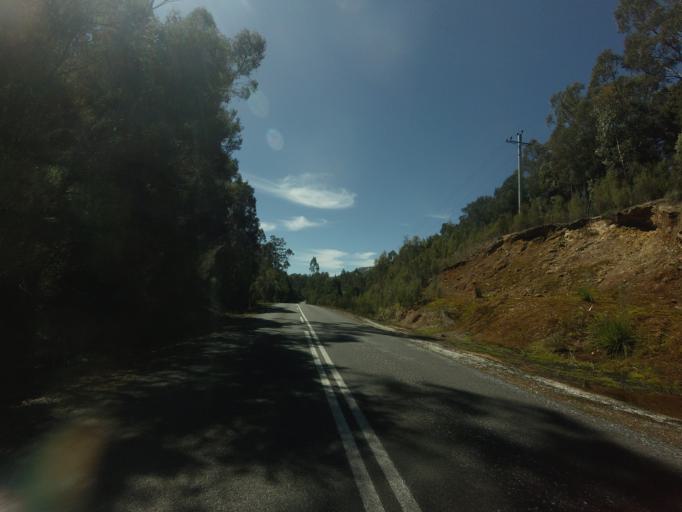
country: AU
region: Tasmania
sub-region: West Coast
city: Queenstown
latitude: -42.7707
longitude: 146.0433
